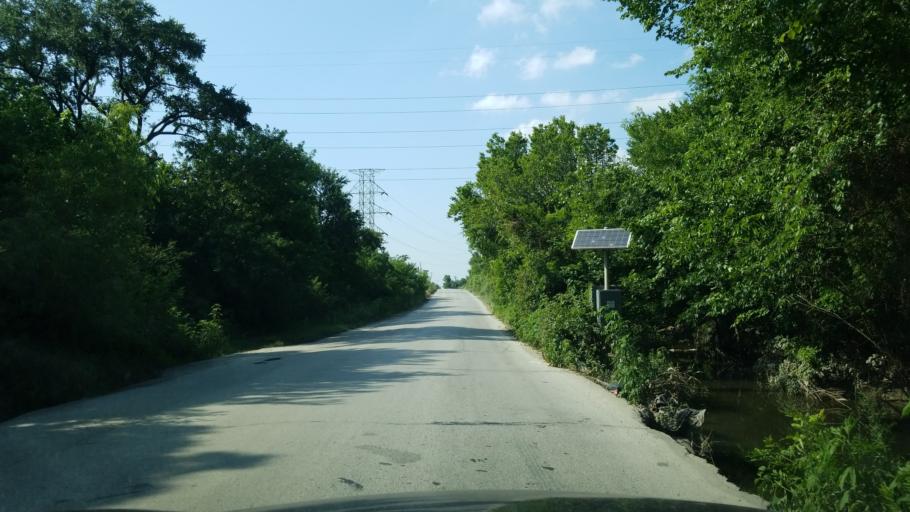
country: US
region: Texas
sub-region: Dallas County
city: Farmers Branch
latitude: 32.8823
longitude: -96.9019
